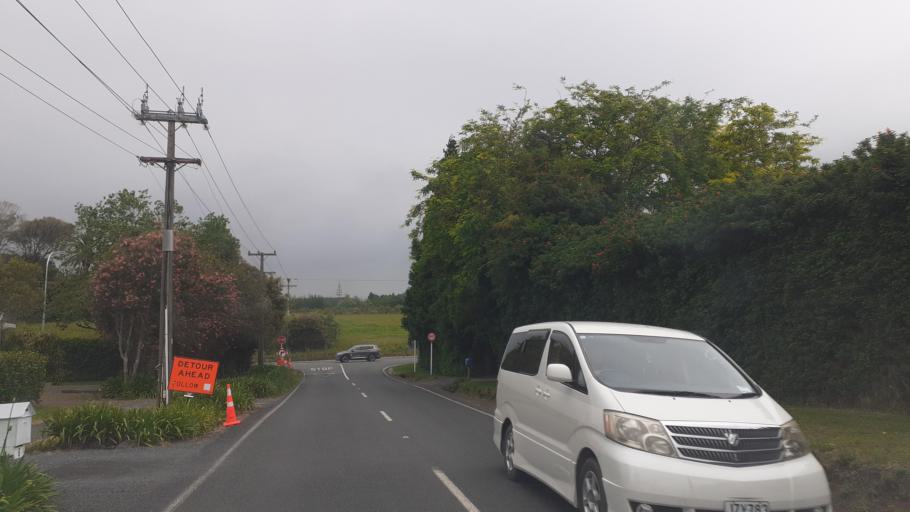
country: NZ
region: Northland
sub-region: Far North District
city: Kerikeri
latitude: -35.2409
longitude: 173.9363
